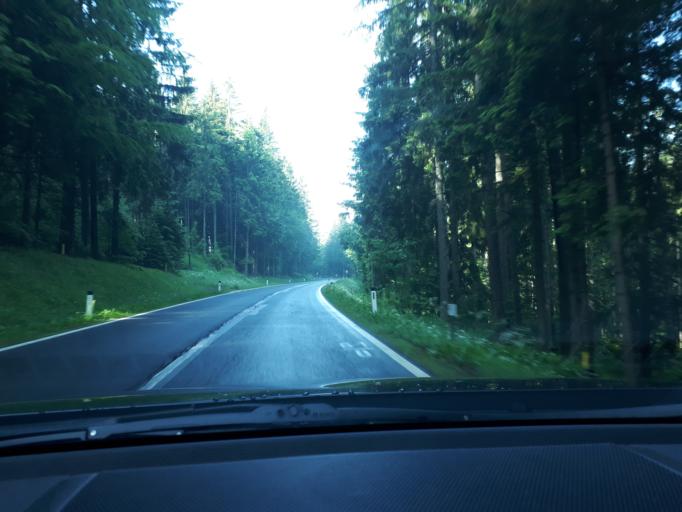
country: AT
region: Styria
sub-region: Politischer Bezirk Voitsberg
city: Pack
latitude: 46.9616
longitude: 14.9757
